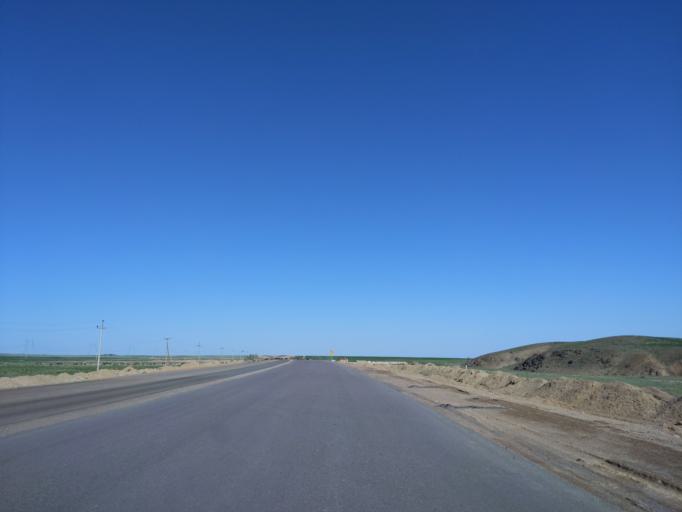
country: KZ
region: Almaty Oblysy
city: Bakanas
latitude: 44.0934
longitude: 75.9885
